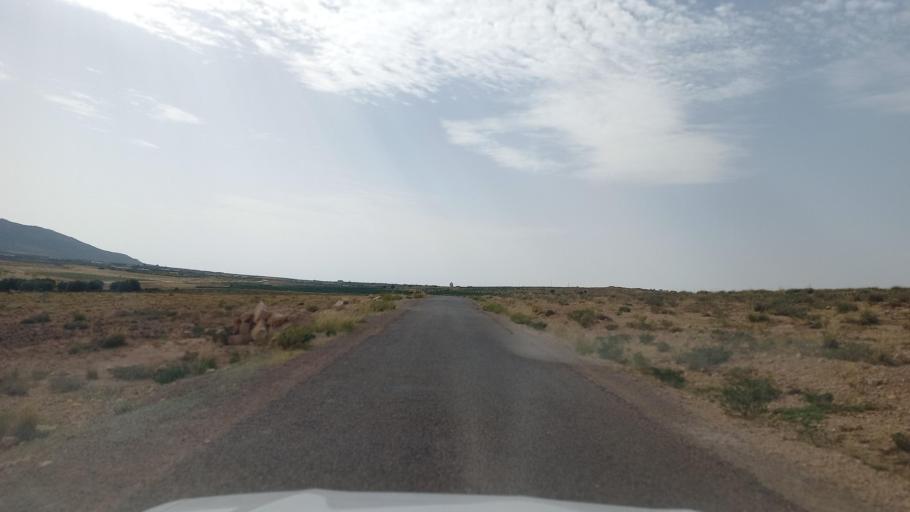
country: TN
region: Al Qasrayn
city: Kasserine
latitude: 35.3600
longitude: 8.8346
